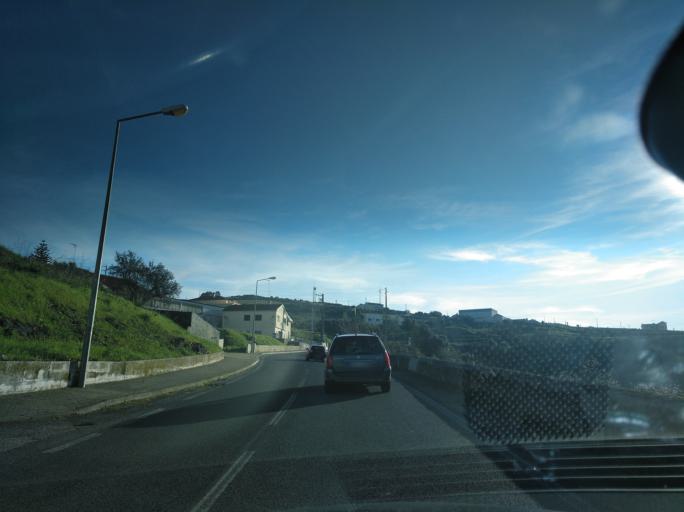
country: PT
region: Lisbon
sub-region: Sintra
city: Pero Pinheiro
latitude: 38.8864
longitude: -9.3306
